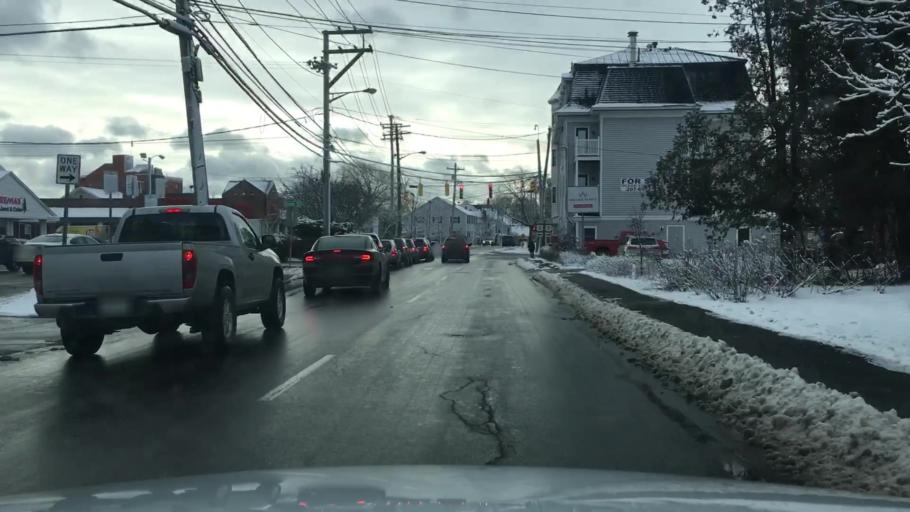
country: US
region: Maine
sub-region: Knox County
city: Rockland
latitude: 44.1028
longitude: -69.1108
